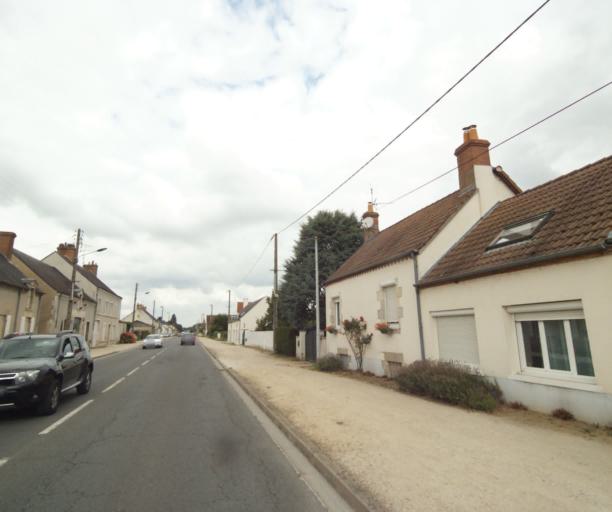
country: FR
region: Centre
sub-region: Departement du Loiret
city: Checy
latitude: 47.8975
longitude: 2.0229
